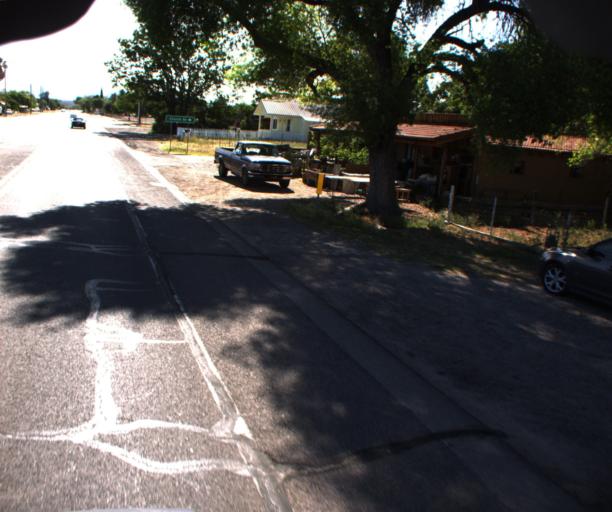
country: US
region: Arizona
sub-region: Cochise County
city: Saint David
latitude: 31.9052
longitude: -110.2250
